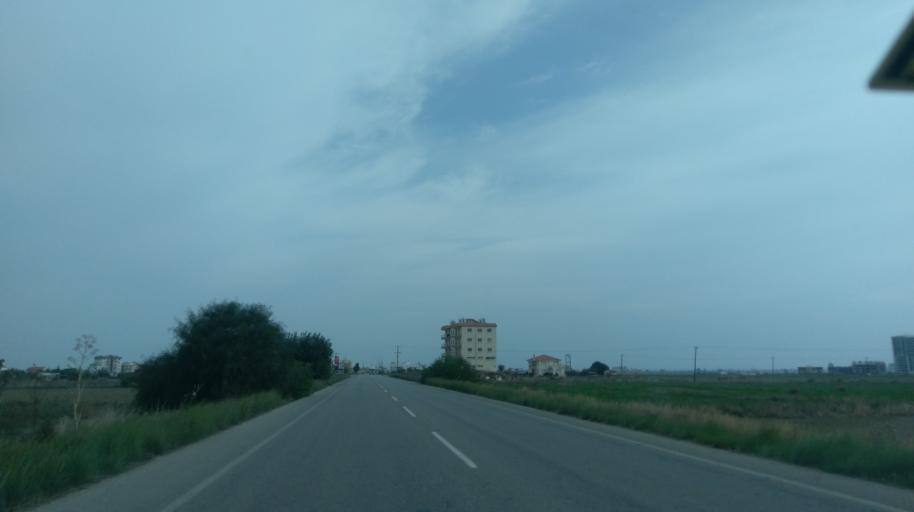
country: CY
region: Ammochostos
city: Trikomo
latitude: 35.2791
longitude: 33.8884
